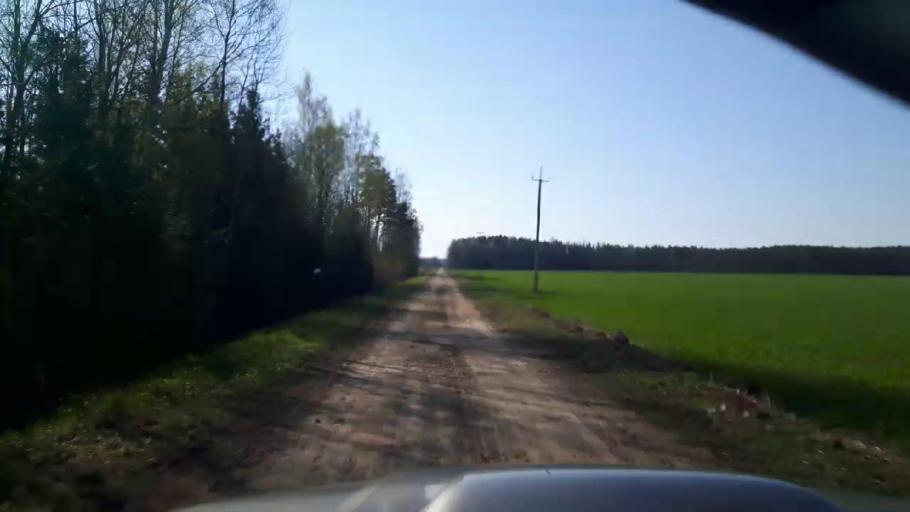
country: EE
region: Paernumaa
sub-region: Tootsi vald
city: Tootsi
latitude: 58.5124
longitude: 24.9308
